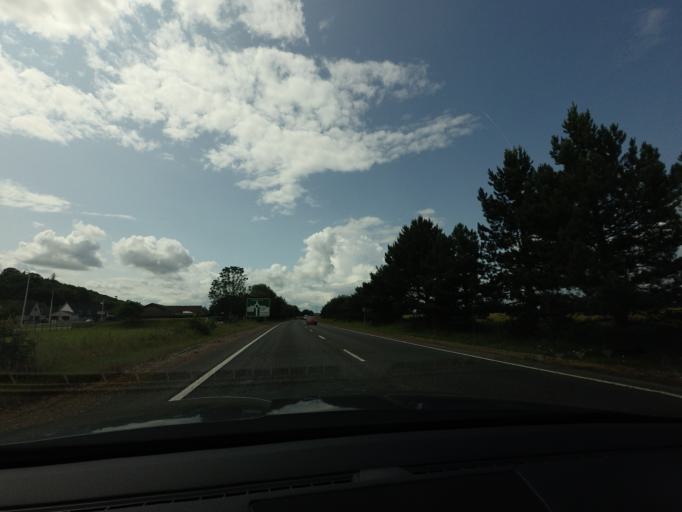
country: GB
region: Scotland
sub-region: Moray
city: Kinloss
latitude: 57.6160
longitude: -3.5911
